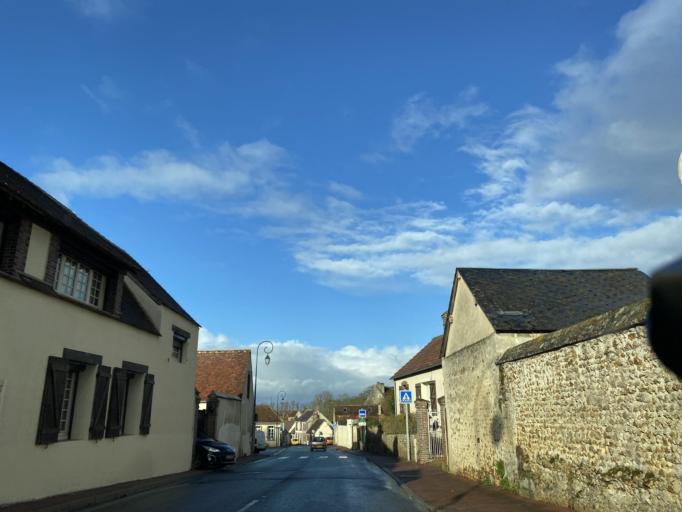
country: FR
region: Centre
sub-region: Departement d'Eure-et-Loir
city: Brezolles
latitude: 48.6277
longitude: 1.1493
